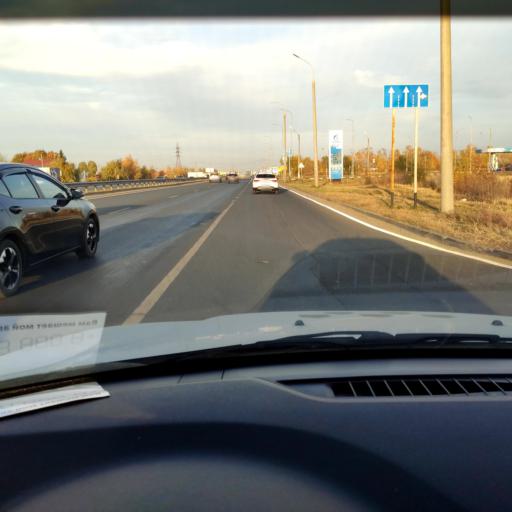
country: RU
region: Samara
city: Tol'yatti
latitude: 53.5586
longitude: 49.3546
